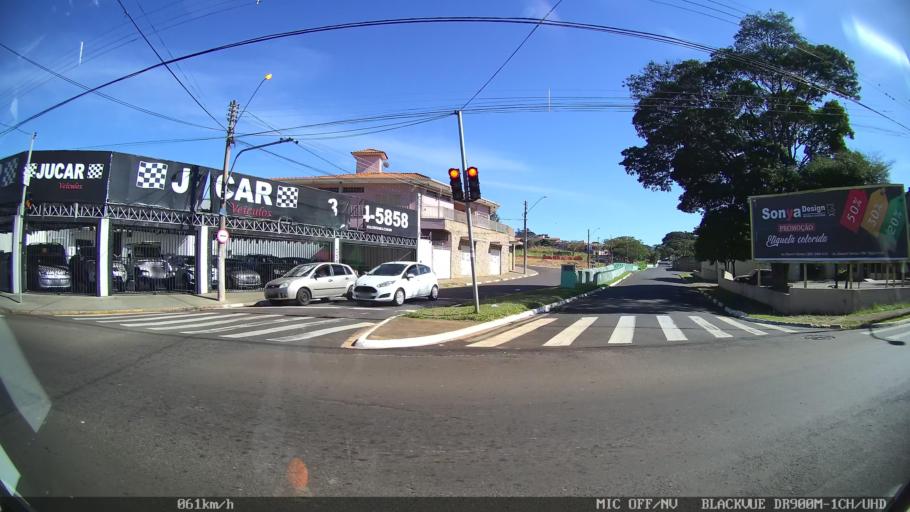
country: BR
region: Sao Paulo
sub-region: Franca
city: Franca
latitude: -20.5226
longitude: -47.4004
